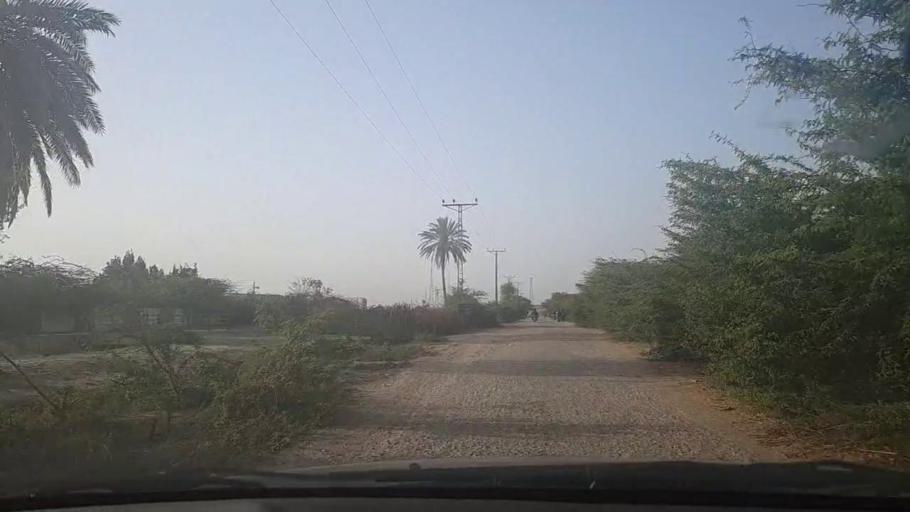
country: PK
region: Sindh
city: Keti Bandar
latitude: 24.2934
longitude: 67.6085
